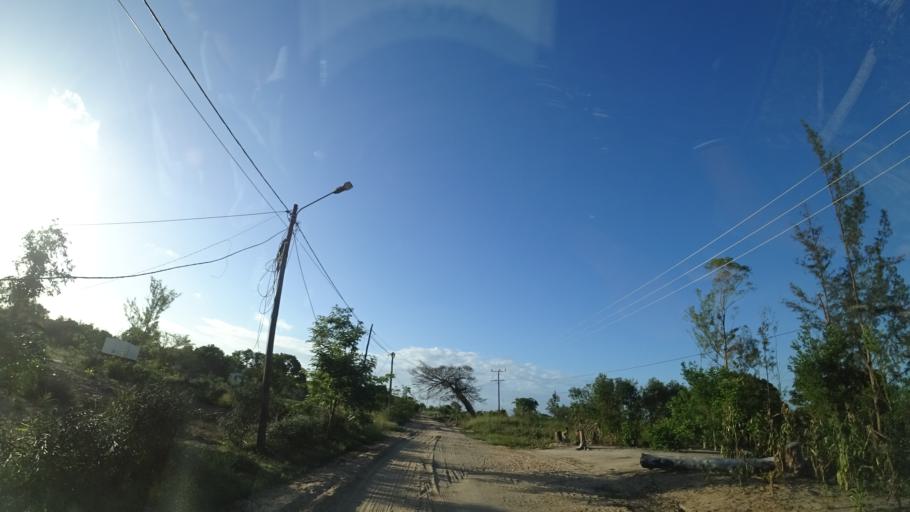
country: MZ
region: Sofala
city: Dondo
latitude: -19.3959
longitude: 34.7088
